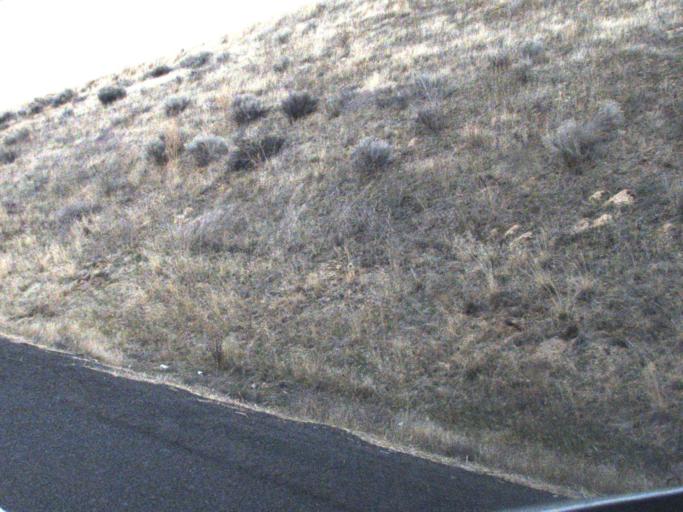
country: US
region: Washington
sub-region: Garfield County
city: Pomeroy
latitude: 46.8043
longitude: -117.7778
